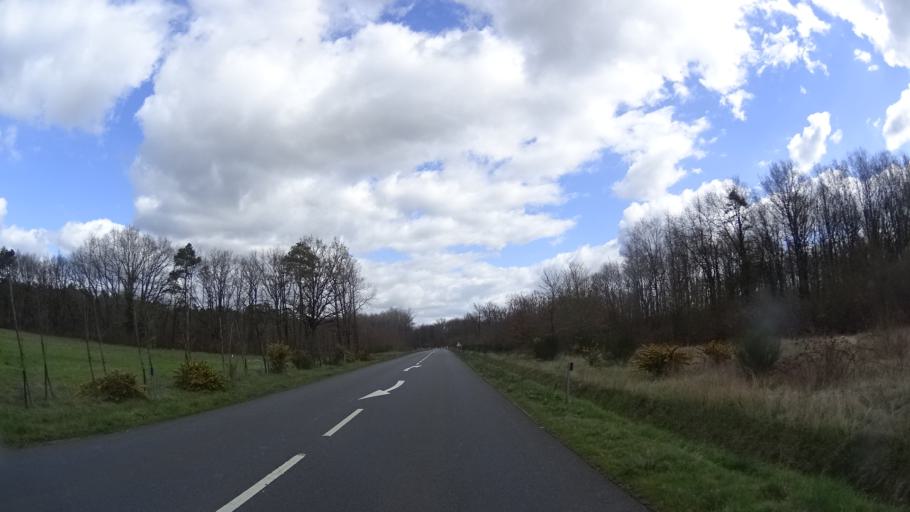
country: FR
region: Pays de la Loire
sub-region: Departement de Maine-et-Loire
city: Breze
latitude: 47.0878
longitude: -0.0070
